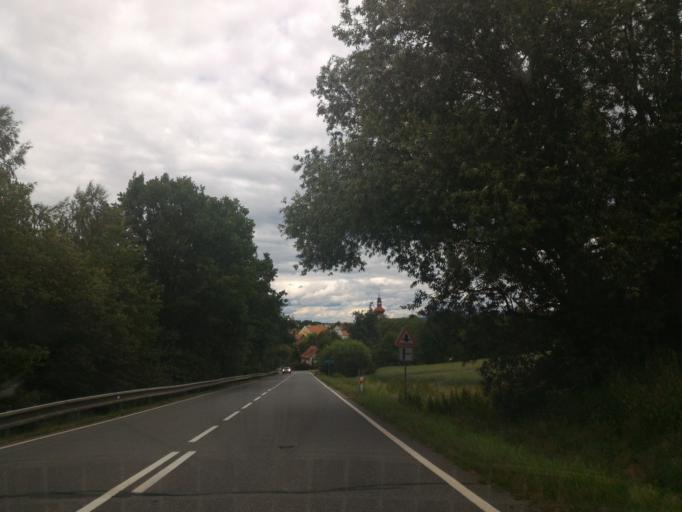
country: CZ
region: Vysocina
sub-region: Okres Pelhrimov
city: Zeliv
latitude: 49.5074
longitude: 15.1782
